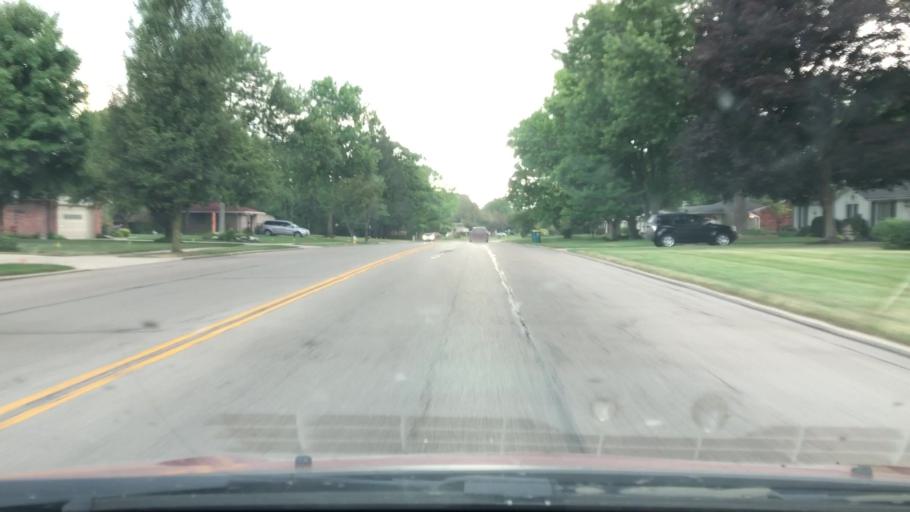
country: US
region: Ohio
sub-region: Greene County
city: Bellbrook
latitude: 39.6618
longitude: -84.1162
